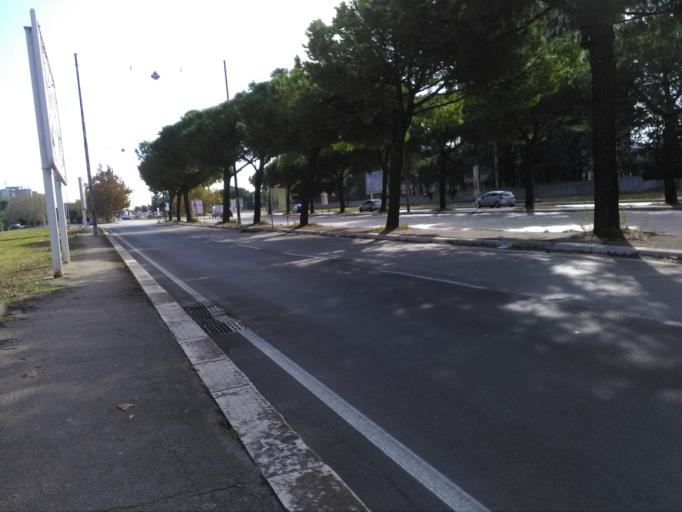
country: IT
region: Apulia
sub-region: Provincia di Bari
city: Triggiano
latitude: 41.1039
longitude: 16.9060
